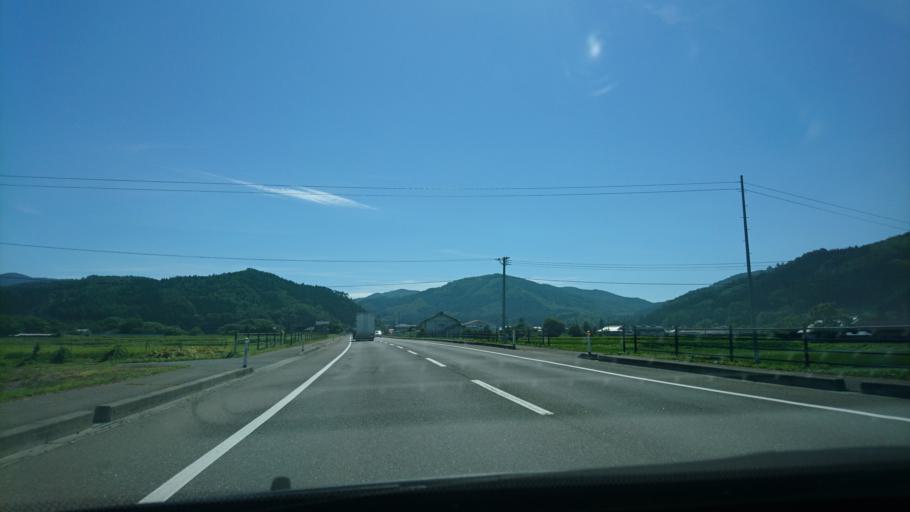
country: JP
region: Iwate
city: Tono
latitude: 39.2735
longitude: 141.5806
